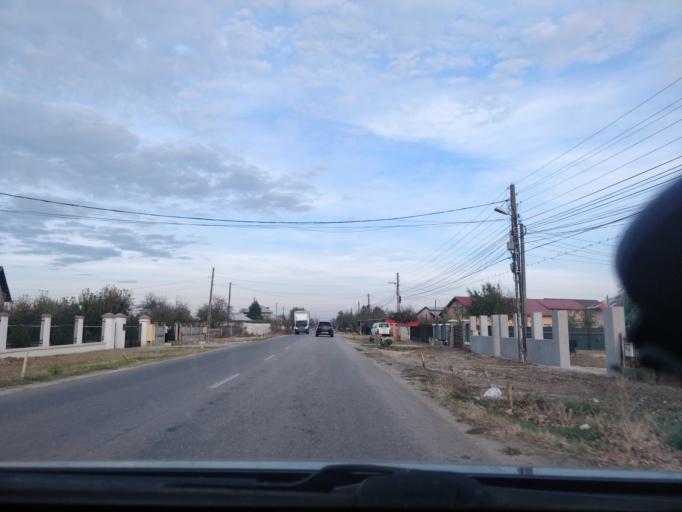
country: RO
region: Giurgiu
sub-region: Comuna Bolintin Vale
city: Malu Spart
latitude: 44.4394
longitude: 25.7005
